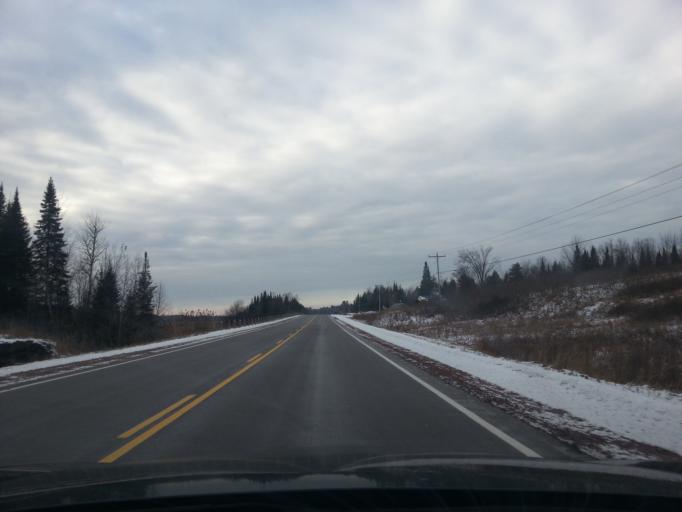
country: CA
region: Ontario
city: Skatepark
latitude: 44.6851
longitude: -77.0384
